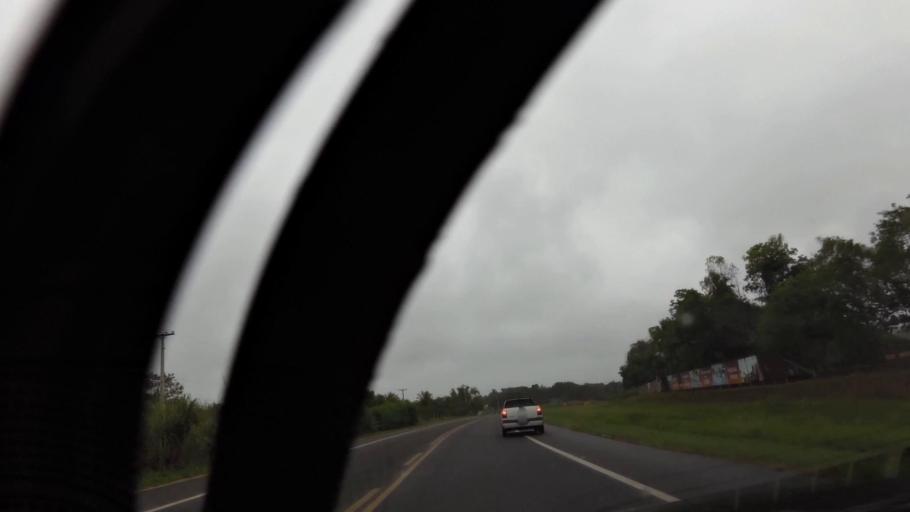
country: BR
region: Espirito Santo
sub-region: Guarapari
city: Guarapari
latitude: -20.7257
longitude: -40.5681
